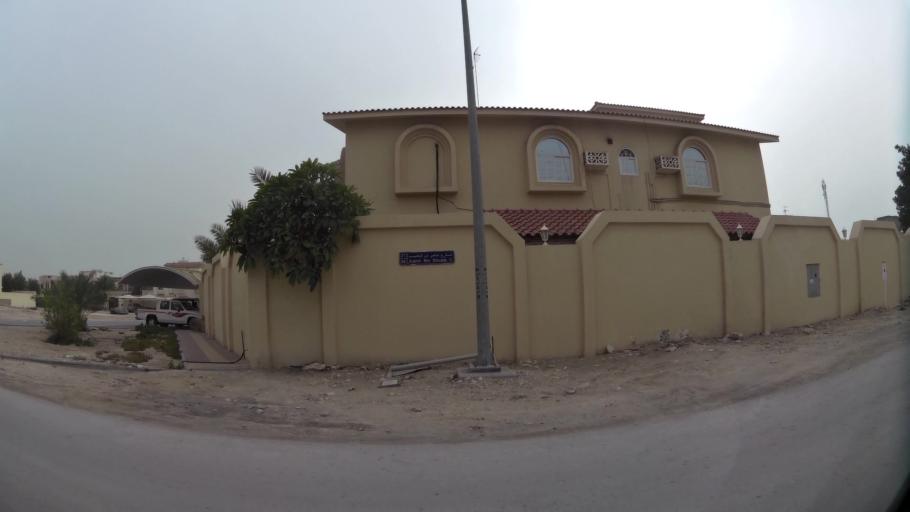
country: QA
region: Baladiyat ad Dawhah
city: Doha
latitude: 25.2494
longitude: 51.4926
